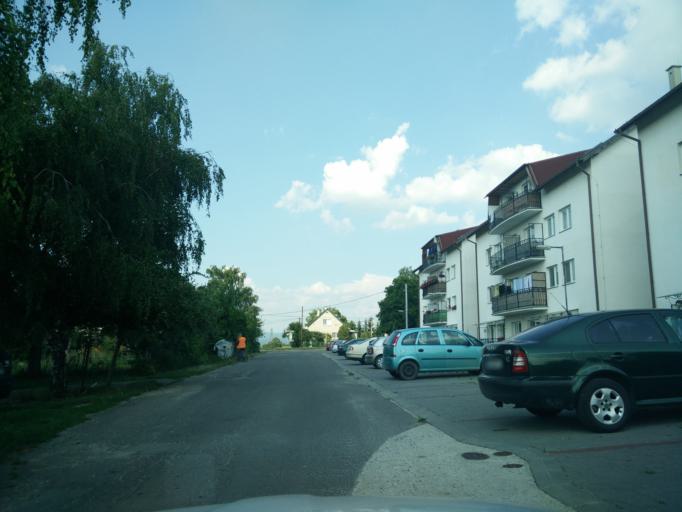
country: SK
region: Nitriansky
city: Prievidza
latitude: 48.7378
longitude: 18.5989
